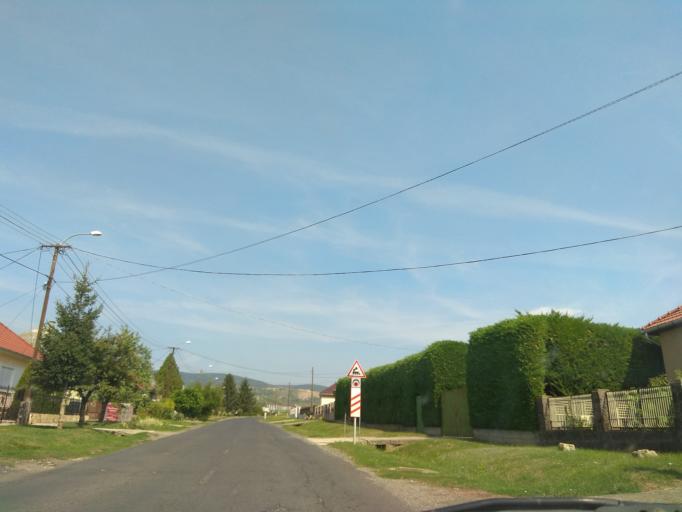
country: HU
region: Borsod-Abauj-Zemplen
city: Tallya
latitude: 48.2210
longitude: 21.2273
